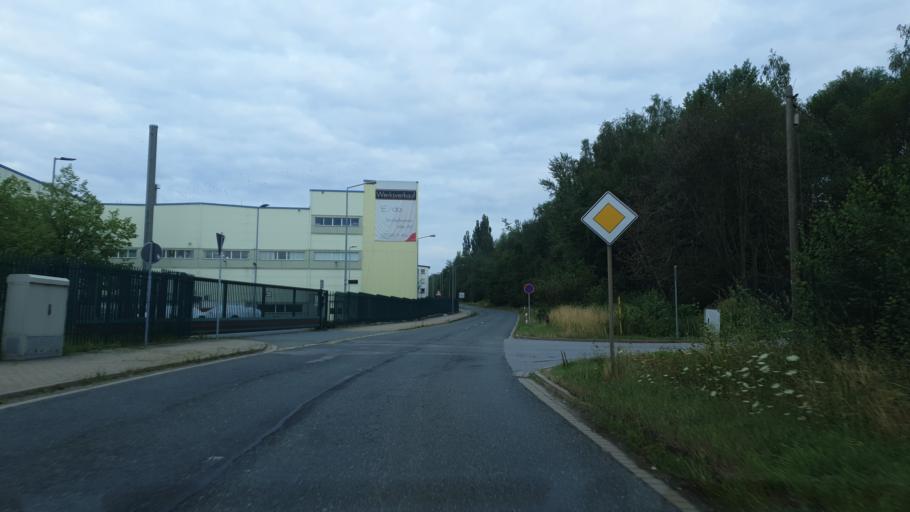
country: DE
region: Saxony
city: Sankt Egidien
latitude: 50.7924
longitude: 12.6231
